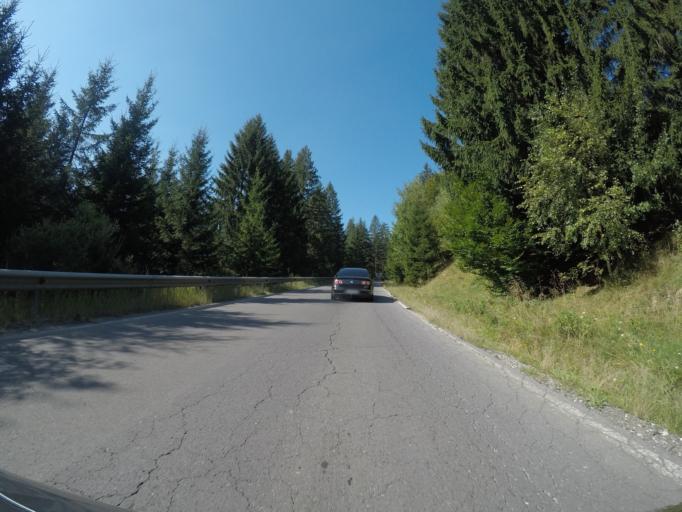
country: RO
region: Brasov
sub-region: Comuna Cristian
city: Cristian
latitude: 45.5888
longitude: 25.5221
